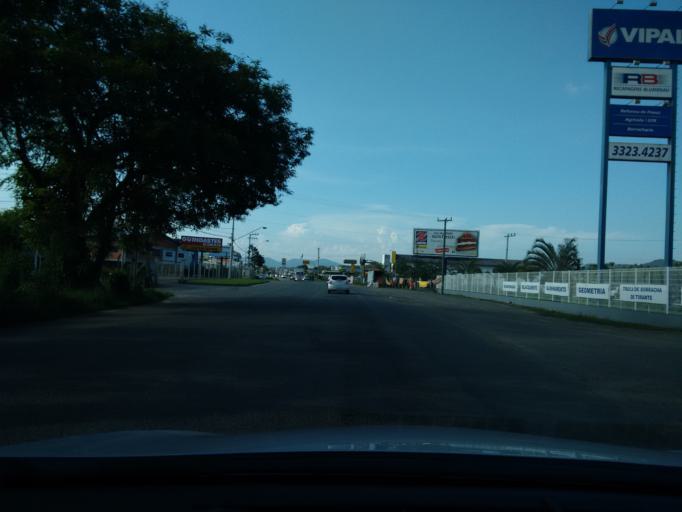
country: BR
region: Santa Catarina
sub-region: Blumenau
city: Blumenau
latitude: -26.8570
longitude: -49.0860
